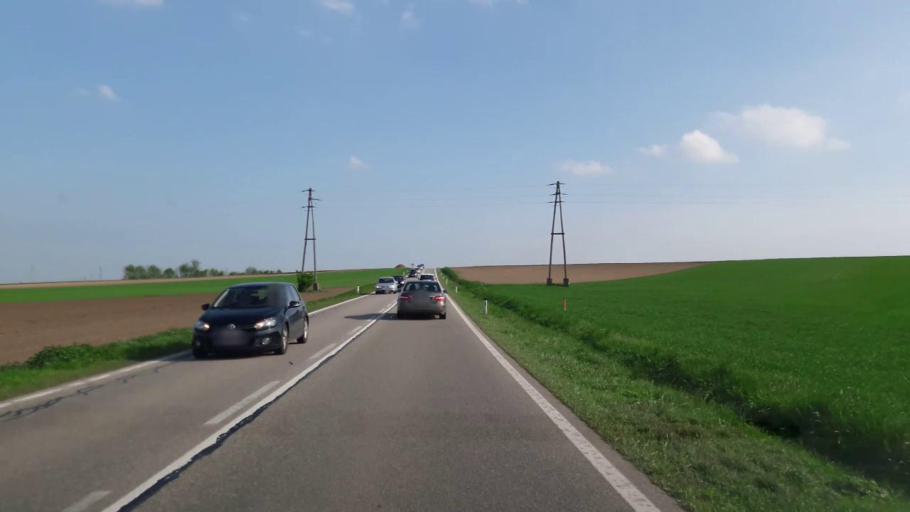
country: AT
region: Lower Austria
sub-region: Politischer Bezirk Hollabrunn
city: Guntersdorf
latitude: 48.6237
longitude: 16.0647
